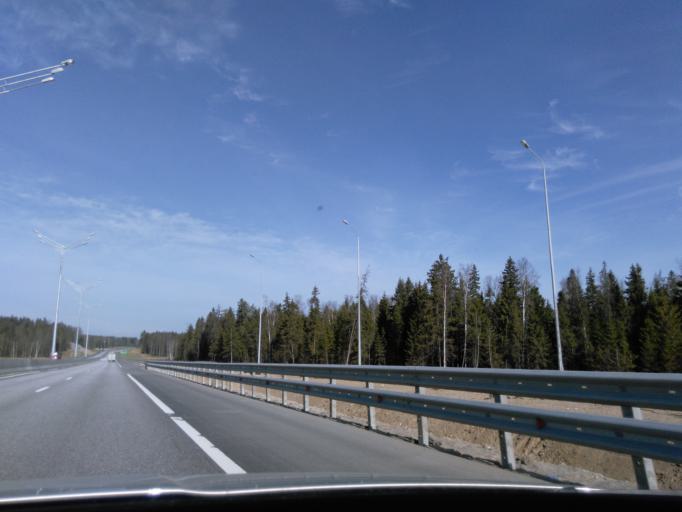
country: RU
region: Moskovskaya
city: Radumlya
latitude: 56.1005
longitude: 37.1626
